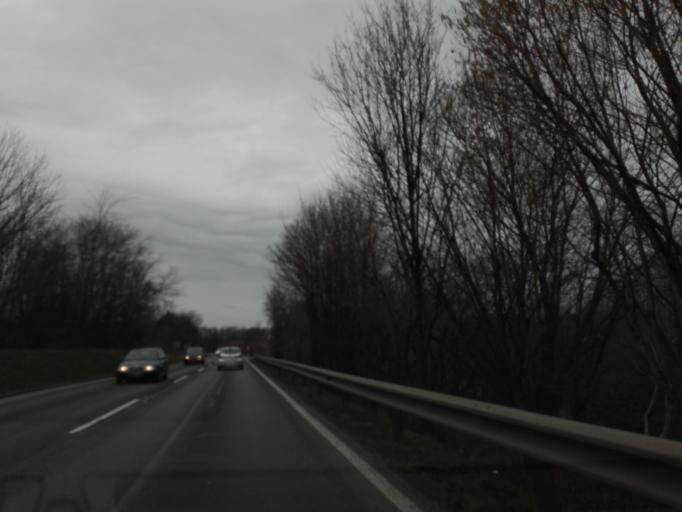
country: AT
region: Upper Austria
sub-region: Politischer Bezirk Linz-Land
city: Ansfelden
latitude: 48.2159
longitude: 14.2666
